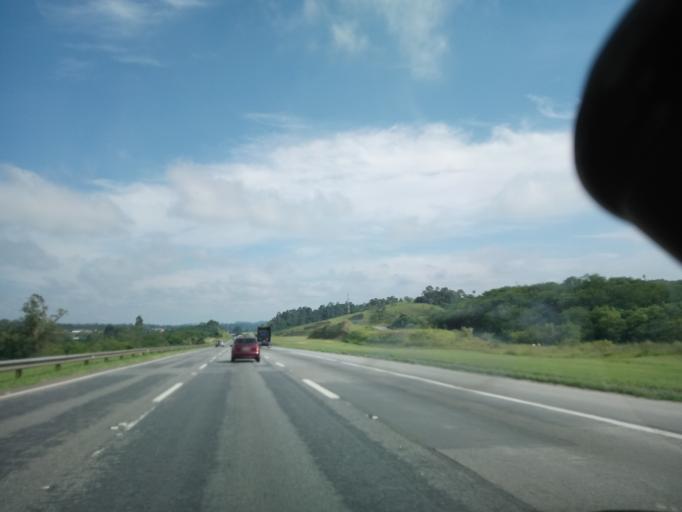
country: BR
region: Sao Paulo
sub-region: Itapecerica Da Serra
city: Itapecerica da Serra
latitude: -23.7066
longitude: -46.8110
